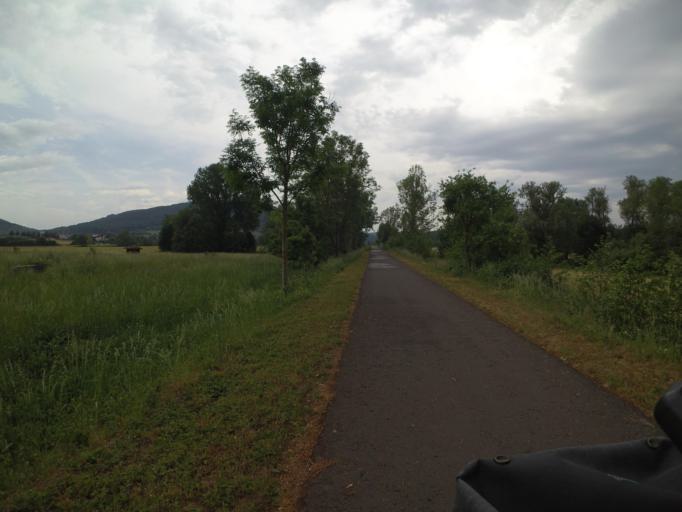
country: DE
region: Rheinland-Pfalz
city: Platten
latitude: 49.9578
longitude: 6.9448
